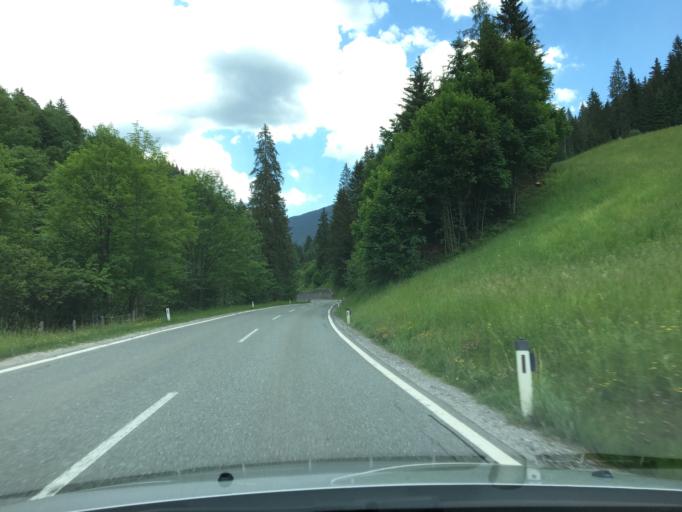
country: AT
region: Salzburg
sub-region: Politischer Bezirk Sankt Johann im Pongau
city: Wagrain
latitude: 47.3359
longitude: 13.2742
